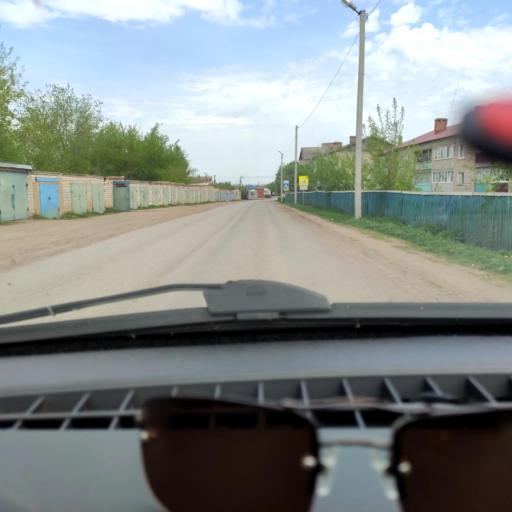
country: RU
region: Bashkortostan
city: Kabakovo
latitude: 54.5319
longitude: 56.1519
